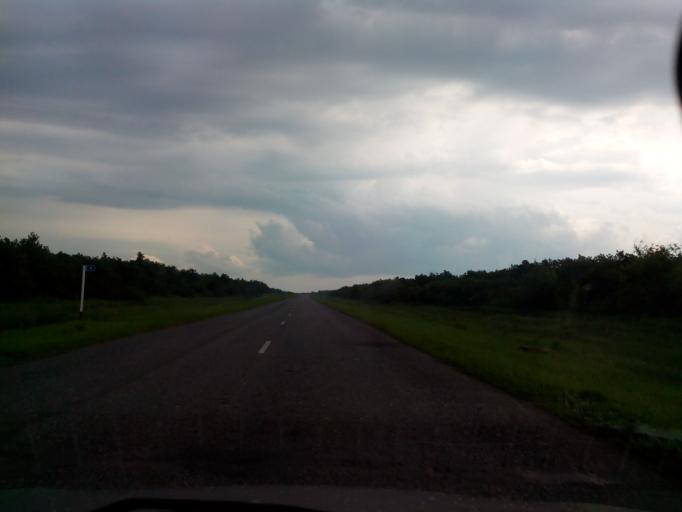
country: RU
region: Volgograd
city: Kumylzhenskaya
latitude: 49.8921
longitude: 42.8110
